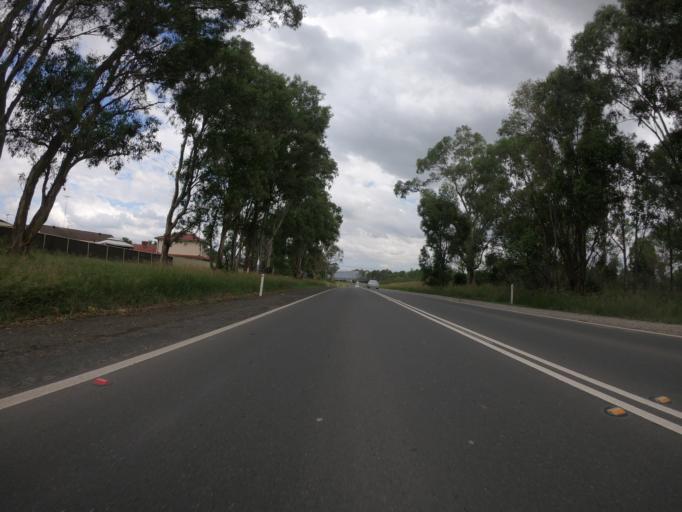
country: AU
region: New South Wales
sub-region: Blacktown
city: Mount Druitt
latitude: -33.8100
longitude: 150.7741
